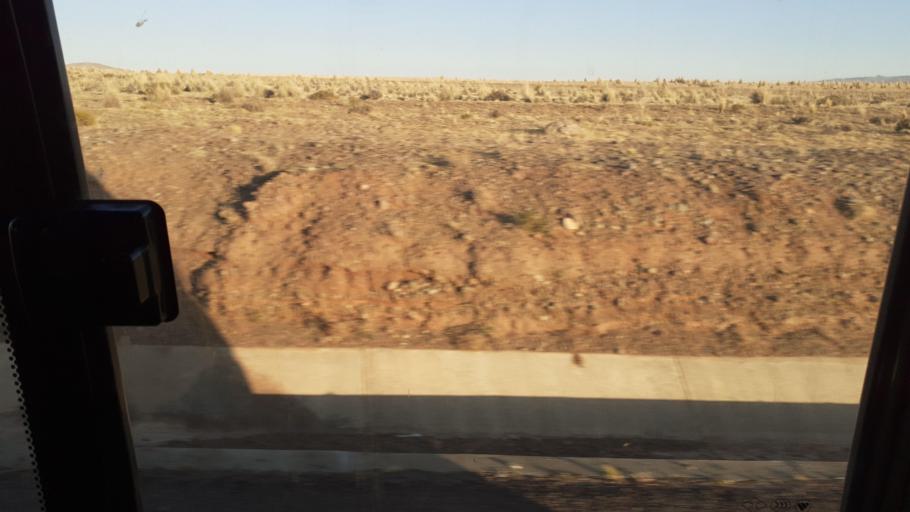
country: BO
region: La Paz
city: Tiahuanaco
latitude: -16.8854
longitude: -68.6830
